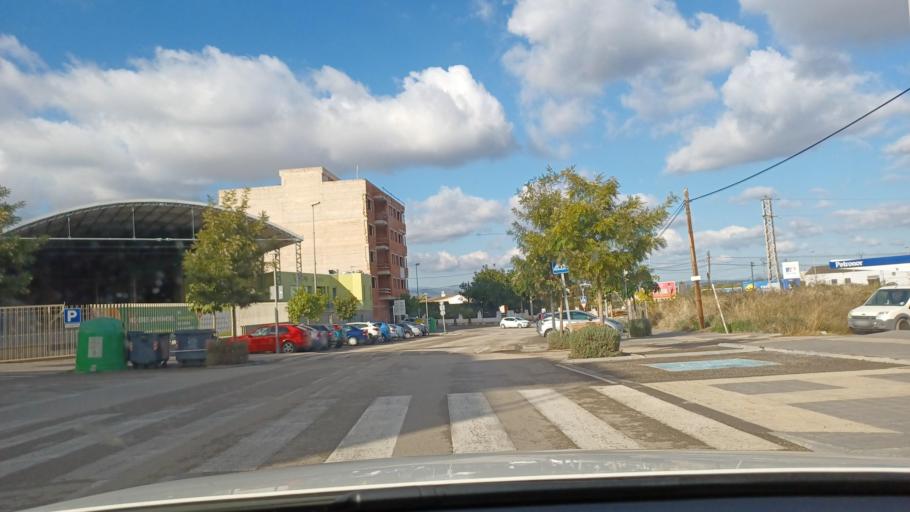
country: ES
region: Valencia
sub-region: Provincia de Castello
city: Betxi
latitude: 39.9301
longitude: -0.1968
